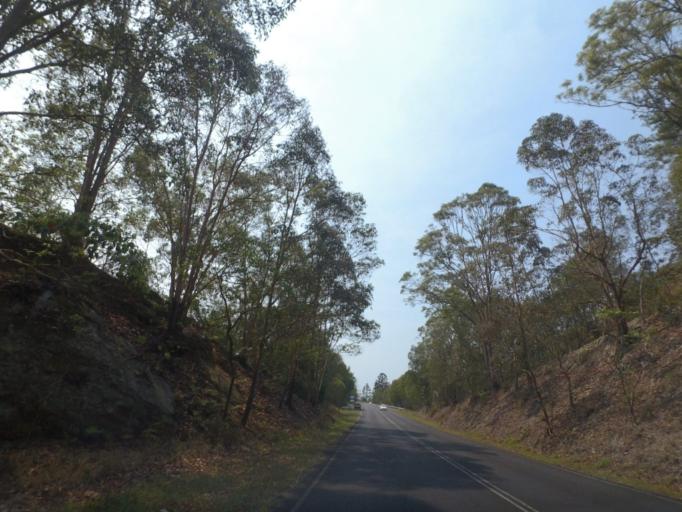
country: AU
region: New South Wales
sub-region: Byron Shire
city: Brunswick Heads
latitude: -28.4954
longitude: 153.5262
